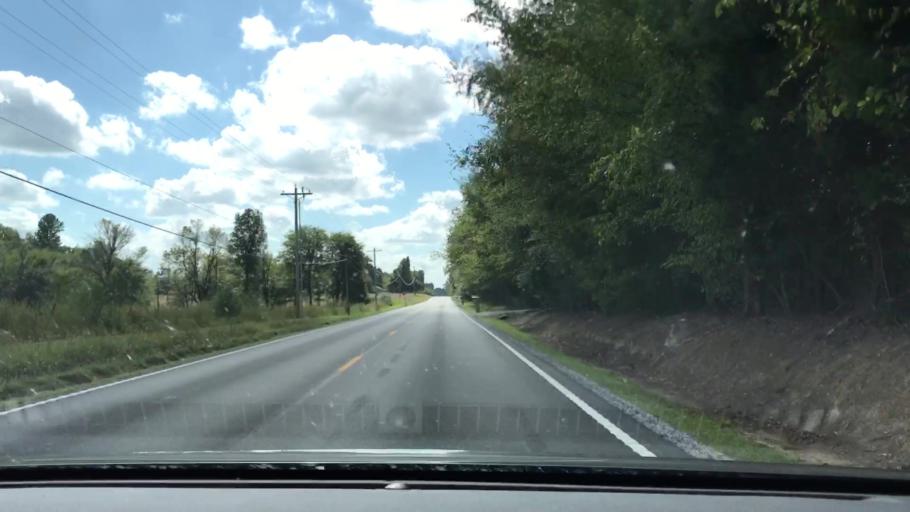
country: US
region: Kentucky
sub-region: Graves County
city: Mayfield
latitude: 36.7987
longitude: -88.5955
